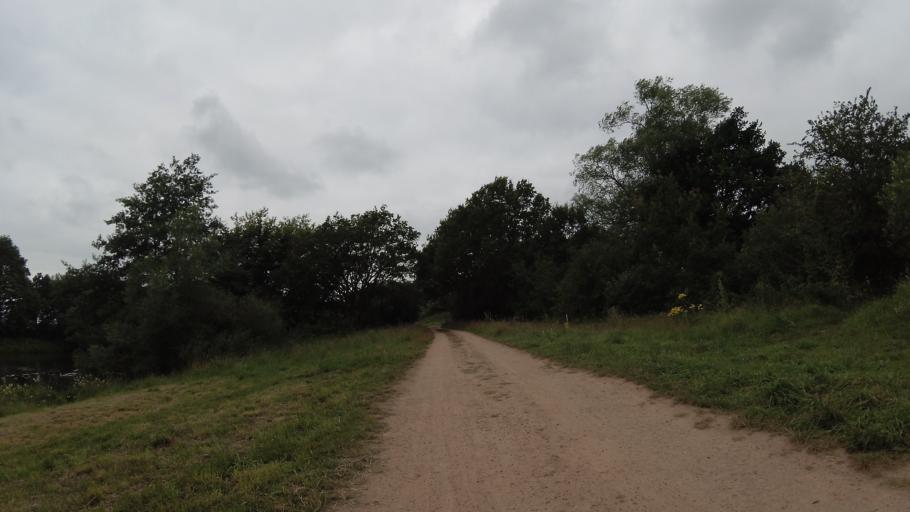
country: DE
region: Lower Saxony
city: Fresenburg
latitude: 52.8721
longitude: 7.3010
